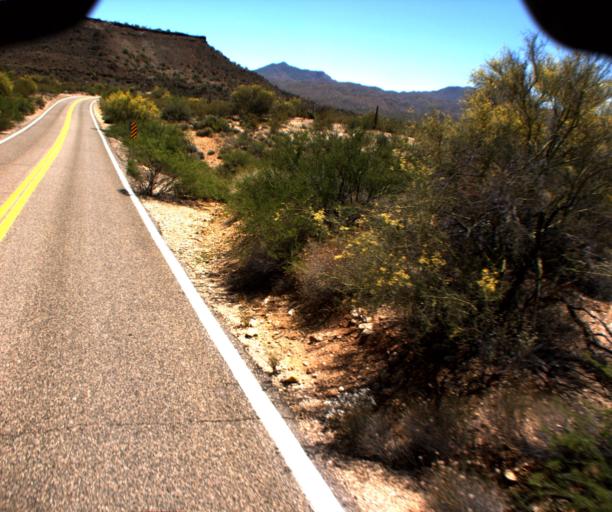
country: US
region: Arizona
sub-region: Yavapai County
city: Bagdad
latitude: 34.4961
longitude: -113.0664
